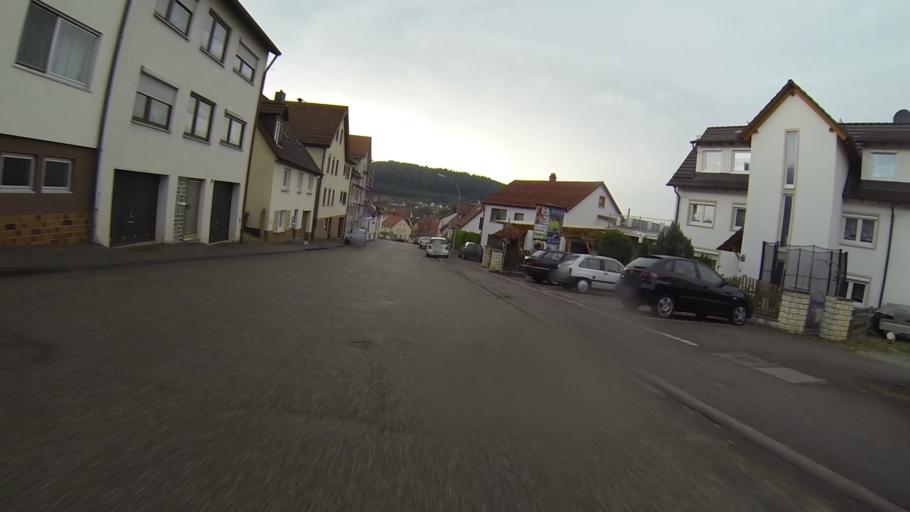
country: DE
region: Baden-Wuerttemberg
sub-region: Regierungsbezirk Stuttgart
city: Heidenheim an der Brenz
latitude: 48.7068
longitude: 10.1673
